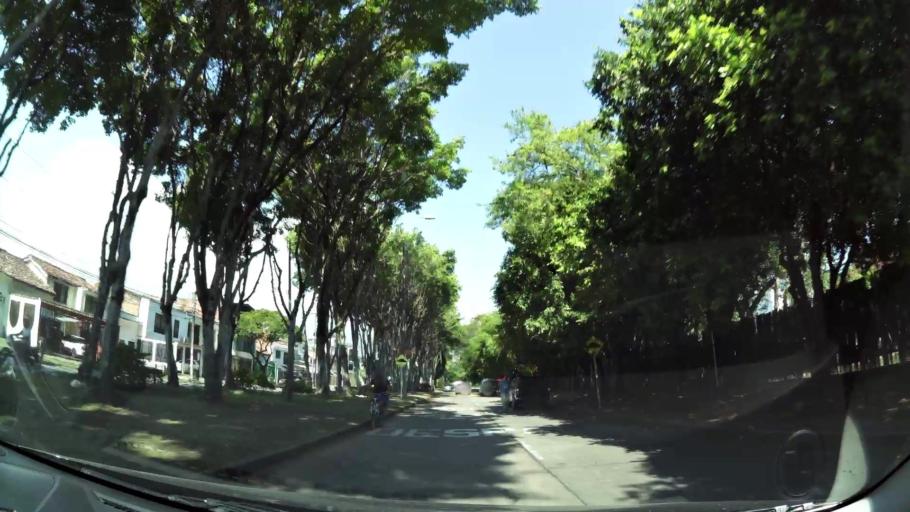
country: CO
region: Valle del Cauca
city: Cali
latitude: 3.4236
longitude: -76.5306
